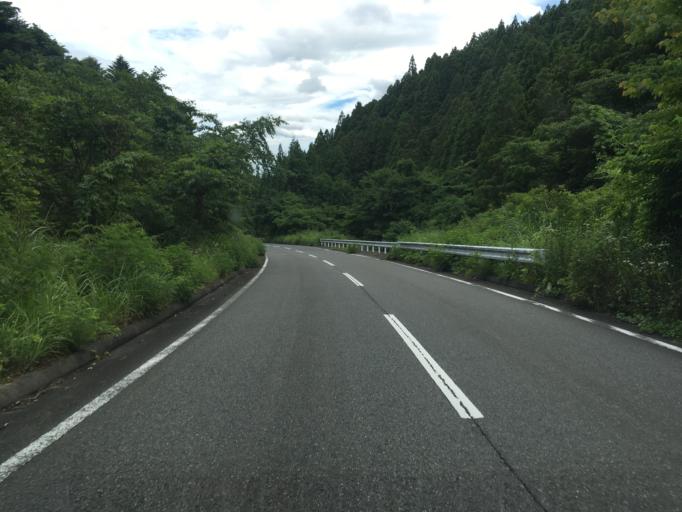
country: JP
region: Miyagi
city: Marumori
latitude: 37.7018
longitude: 140.8786
